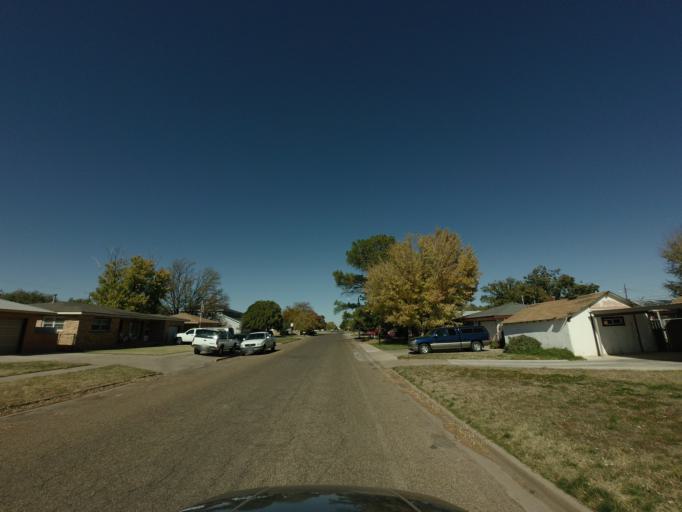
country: US
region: New Mexico
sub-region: Curry County
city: Clovis
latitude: 34.4255
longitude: -103.2003
